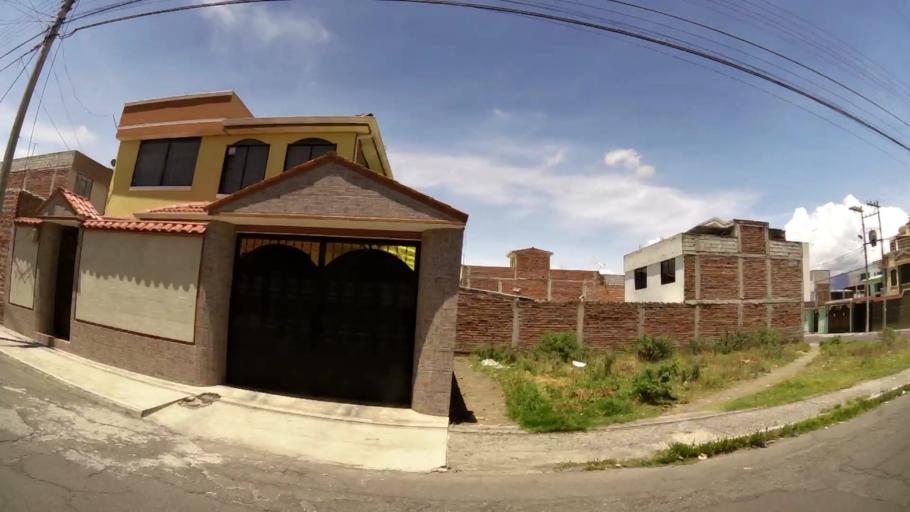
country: EC
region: Chimborazo
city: Riobamba
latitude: -1.6803
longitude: -78.6494
